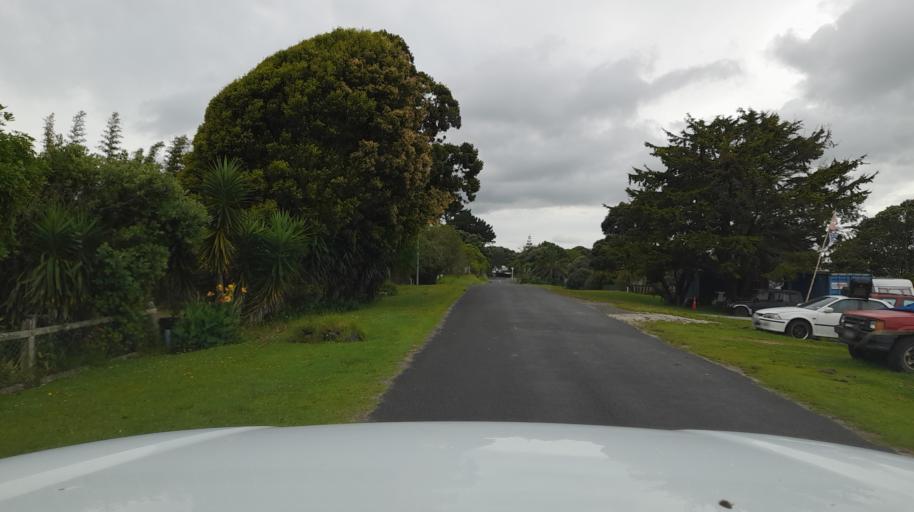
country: NZ
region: Northland
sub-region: Far North District
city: Ahipara
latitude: -35.1626
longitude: 173.1574
